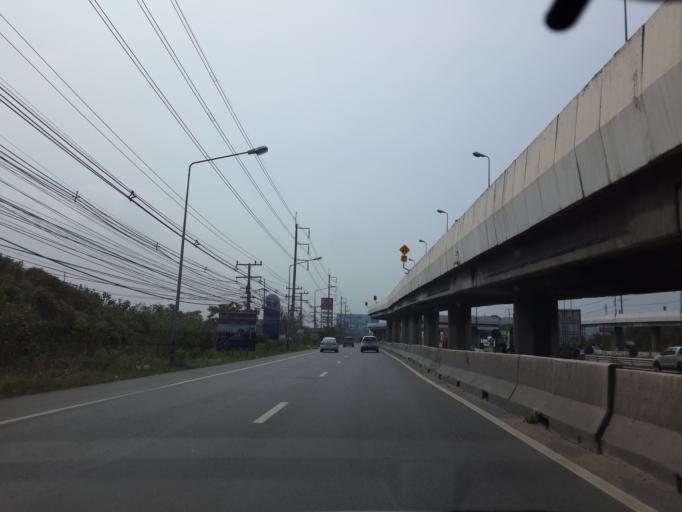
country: TH
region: Chon Buri
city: Chon Buri
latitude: 13.4372
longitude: 101.0015
